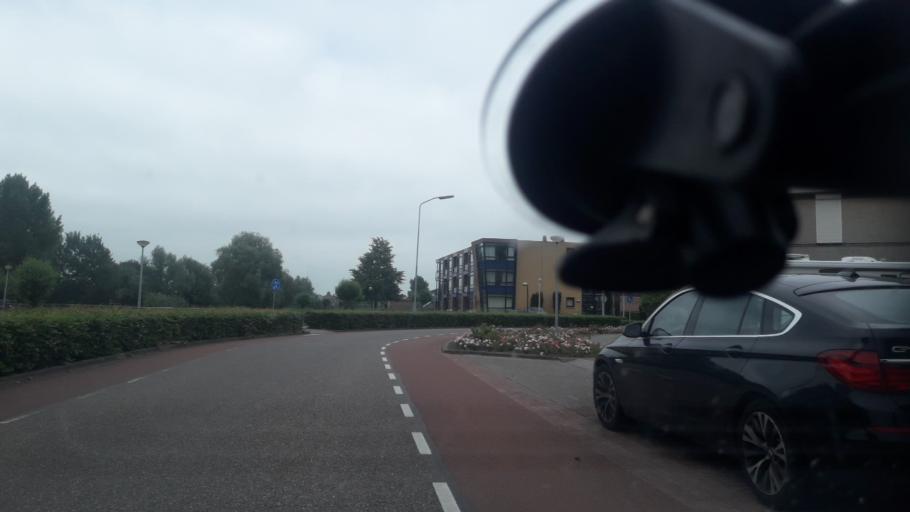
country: NL
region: Gelderland
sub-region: Gemeente Elburg
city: Elburg
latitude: 52.4467
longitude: 5.8549
